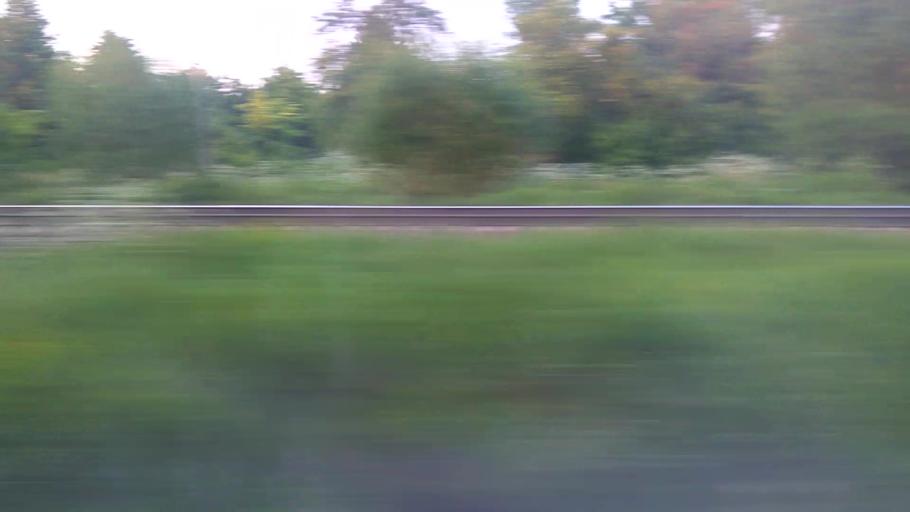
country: RU
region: Moskovskaya
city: Barybino
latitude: 55.2786
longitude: 37.8933
